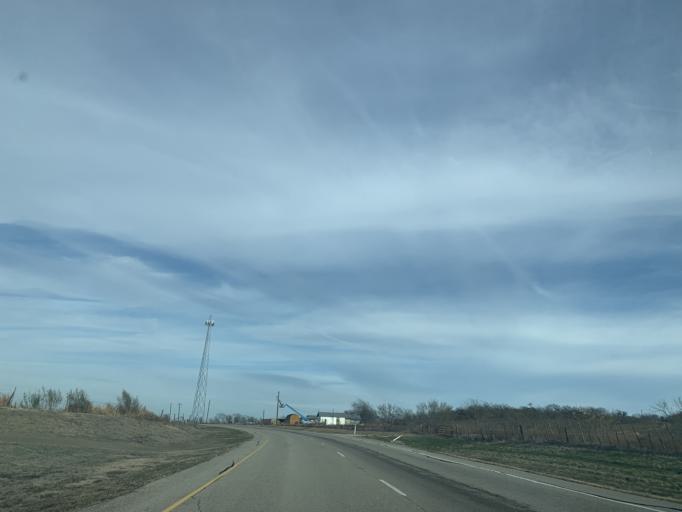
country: US
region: Texas
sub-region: Bell County
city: Salado
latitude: 30.8999
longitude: -97.5603
